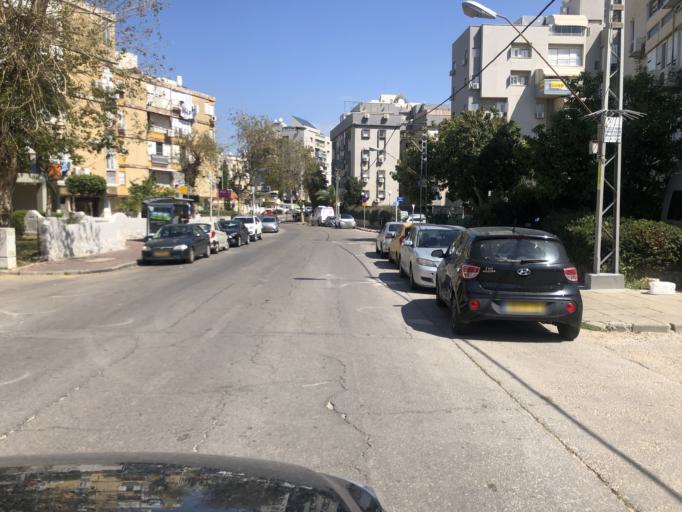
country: IL
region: Tel Aviv
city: Holon
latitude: 32.0027
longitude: 34.7653
